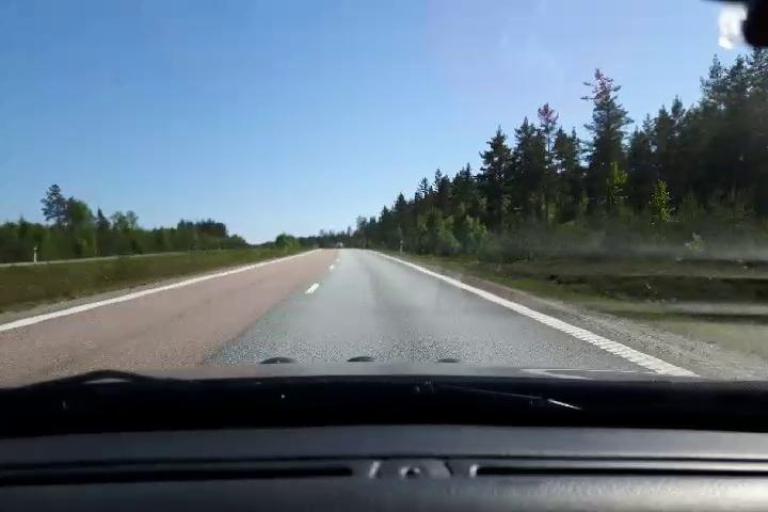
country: SE
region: Gaevleborg
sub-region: Soderhamns Kommun
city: Soderhamn
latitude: 61.4601
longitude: 16.9879
